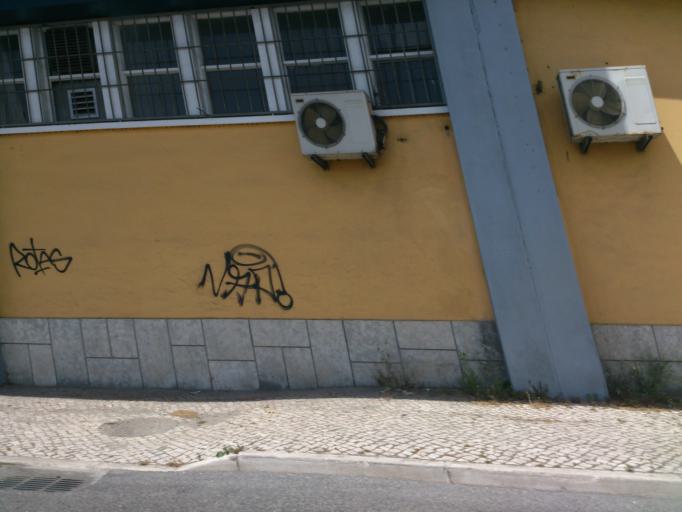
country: PT
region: Lisbon
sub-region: Loures
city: Moscavide
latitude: 38.7400
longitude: -9.1018
